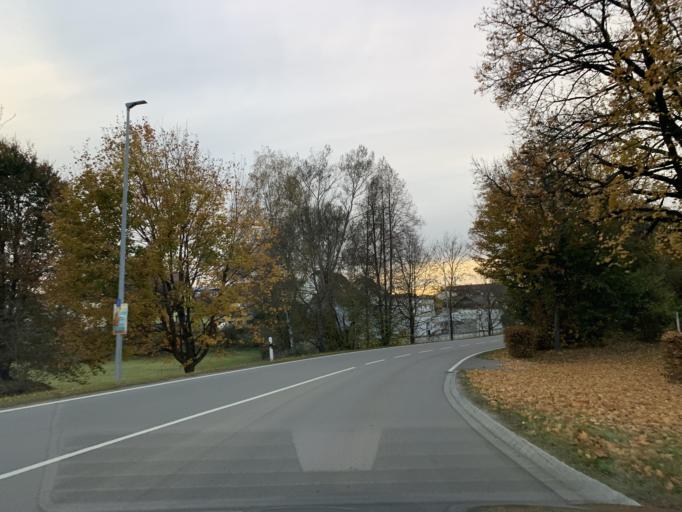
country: DE
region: Bavaria
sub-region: Upper Palatinate
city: Neunburg vorm Wald
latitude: 49.3464
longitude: 12.3861
